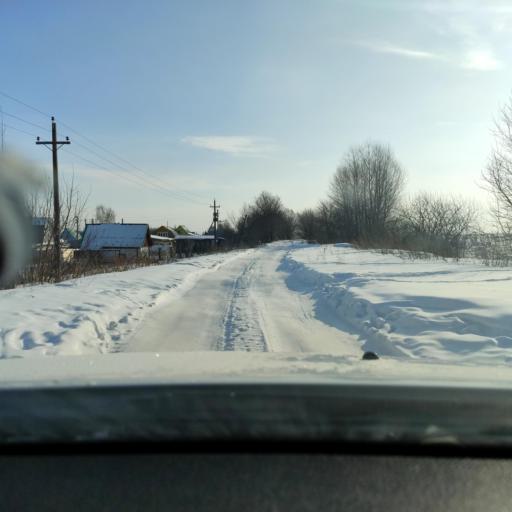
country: RU
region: Bashkortostan
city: Avdon
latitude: 54.7164
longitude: 55.7834
